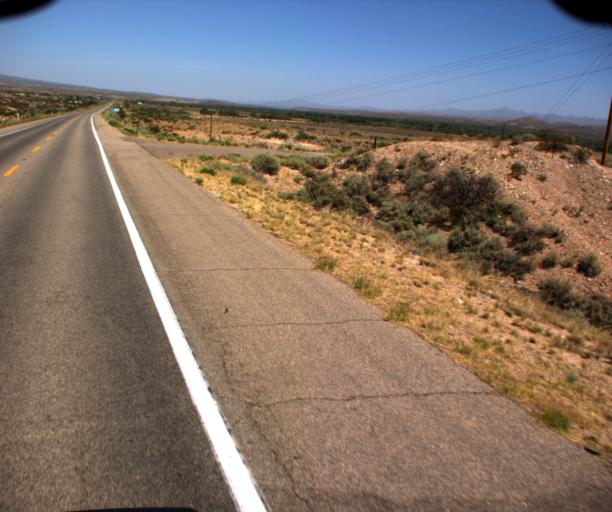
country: US
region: Arizona
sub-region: Graham County
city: Bylas
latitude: 33.0798
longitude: -110.0414
